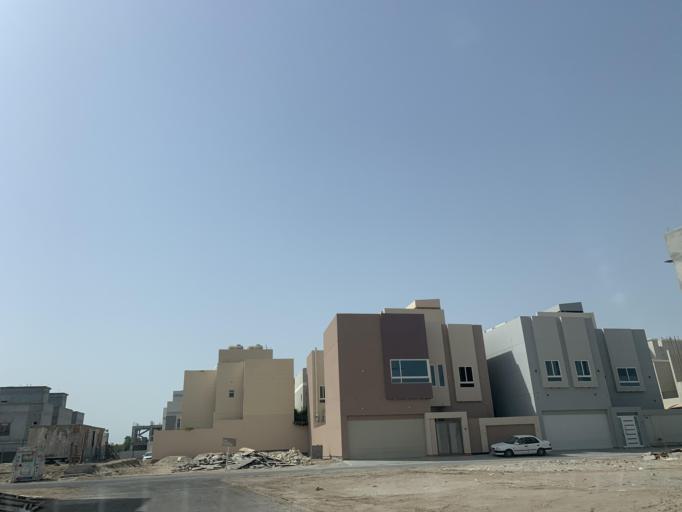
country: BH
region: Manama
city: Jidd Hafs
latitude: 26.2095
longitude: 50.5124
